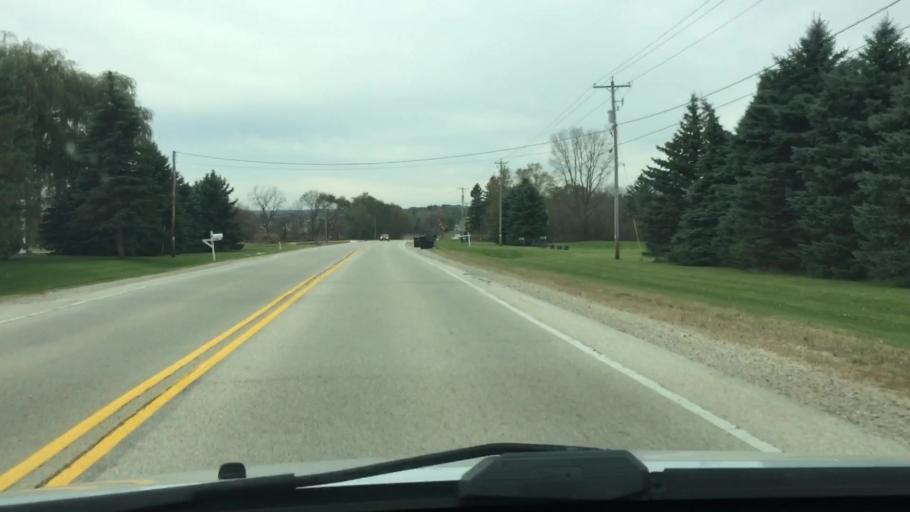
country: US
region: Wisconsin
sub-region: Waukesha County
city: Mukwonago
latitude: 42.8839
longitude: -88.2894
